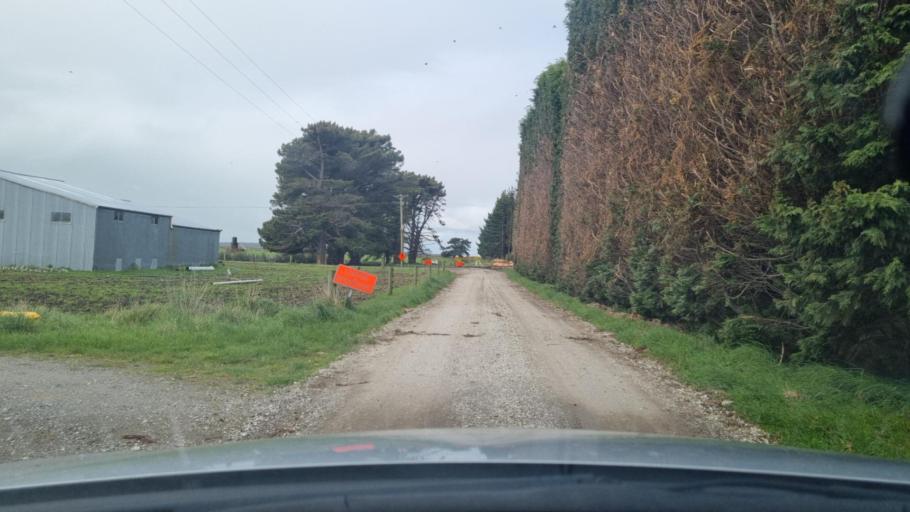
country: NZ
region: Southland
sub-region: Invercargill City
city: Invercargill
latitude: -46.4920
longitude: 168.4376
